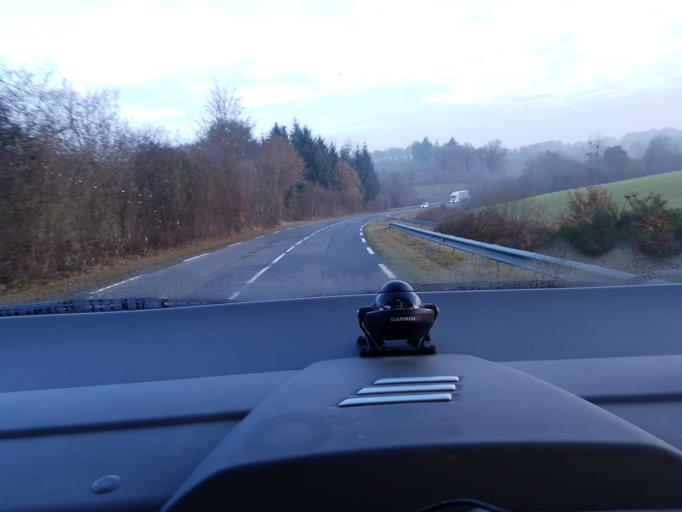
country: FR
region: Lower Normandy
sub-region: Departement de l'Orne
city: Champsecret
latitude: 48.6146
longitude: -0.5867
